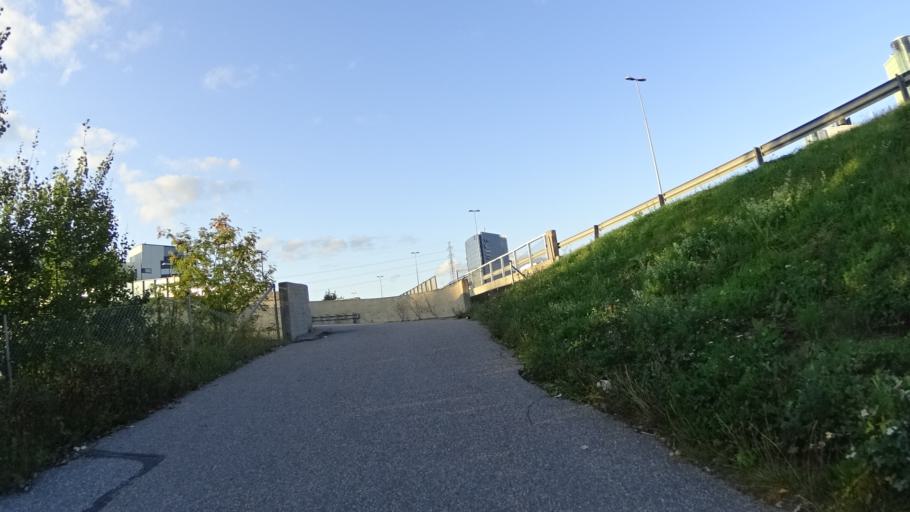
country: FI
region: Uusimaa
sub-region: Helsinki
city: Helsinki
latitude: 60.2189
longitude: 24.9446
